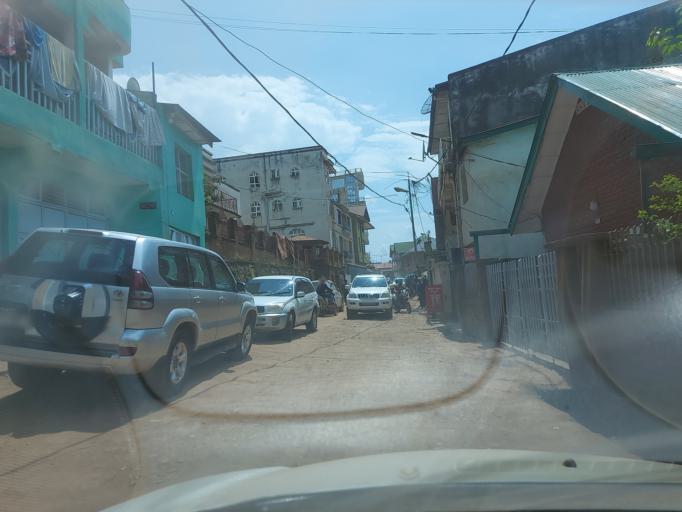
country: CD
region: South Kivu
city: Bukavu
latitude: -2.4986
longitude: 28.8556
